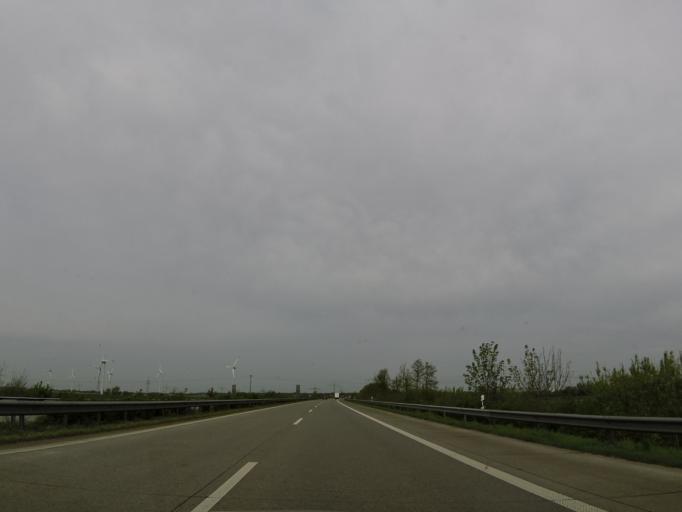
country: DE
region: Schleswig-Holstein
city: Rethwisch
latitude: 53.8484
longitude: 9.5898
